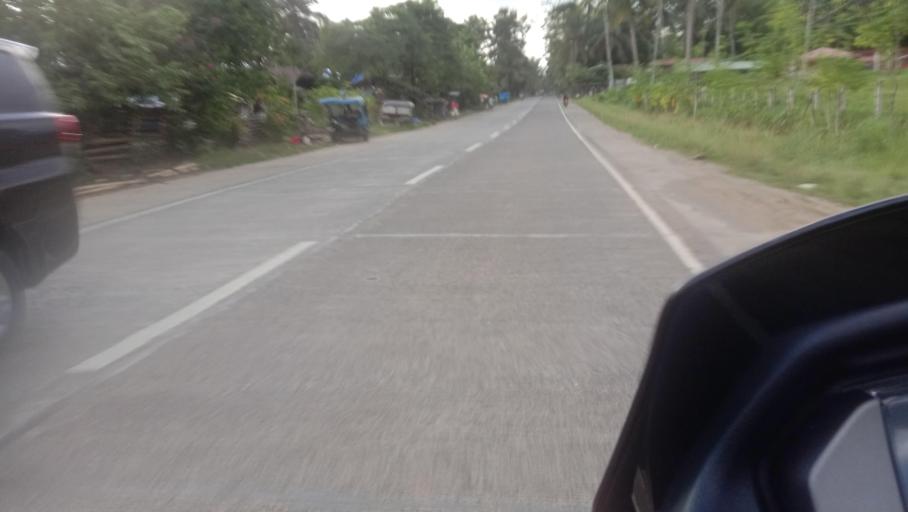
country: PH
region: Caraga
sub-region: Province of Surigao del Sur
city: Barobo
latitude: 8.5148
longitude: 126.1254
